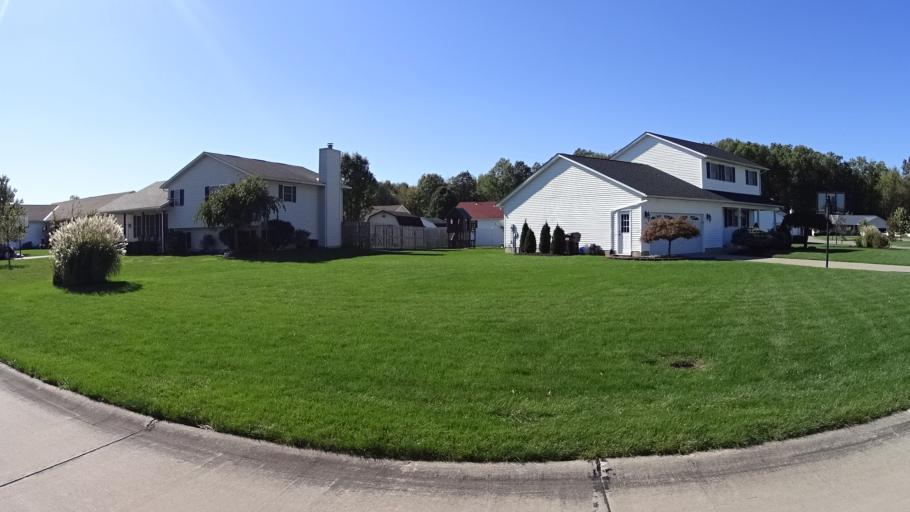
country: US
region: Ohio
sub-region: Lorain County
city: Amherst
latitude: 41.3952
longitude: -82.1979
